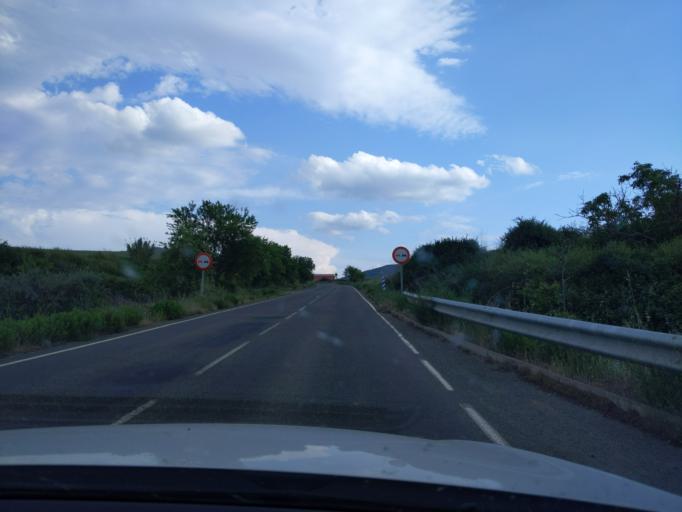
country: ES
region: La Rioja
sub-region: Provincia de La Rioja
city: Alberite
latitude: 42.3844
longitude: -2.4240
